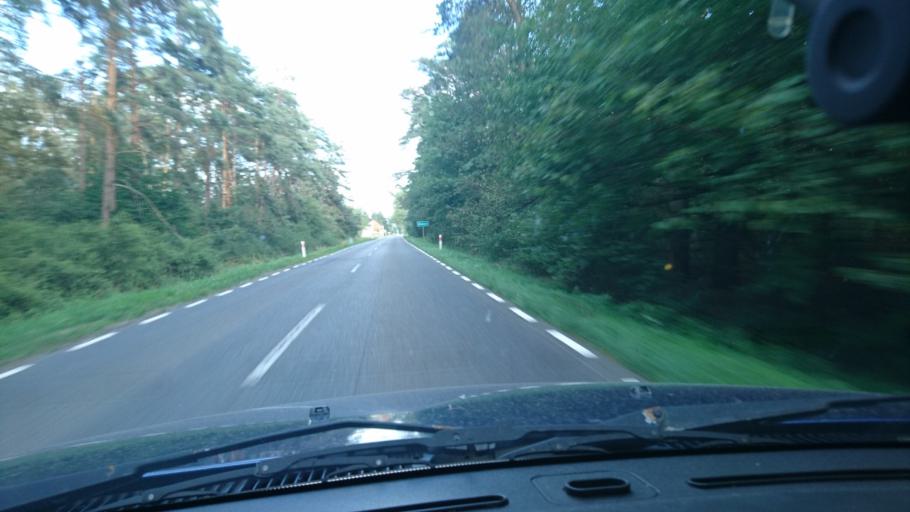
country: PL
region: Greater Poland Voivodeship
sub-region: Powiat ostrowski
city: Odolanow
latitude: 51.5965
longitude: 17.6129
